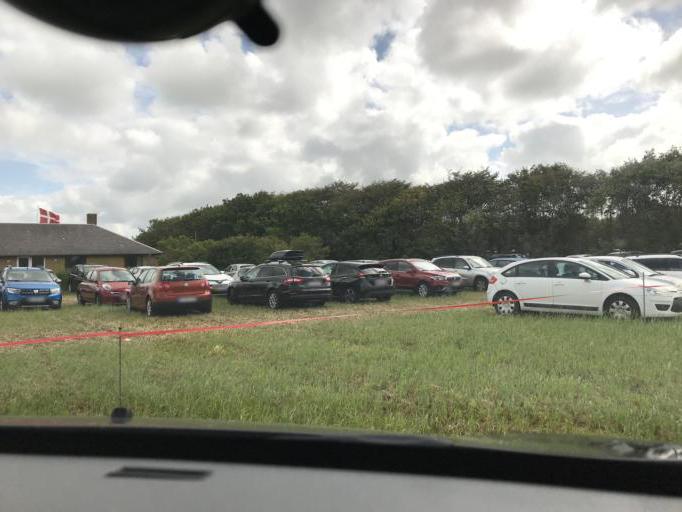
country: DK
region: South Denmark
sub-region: Varde Kommune
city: Oksbol
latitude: 55.7083
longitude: 8.2984
